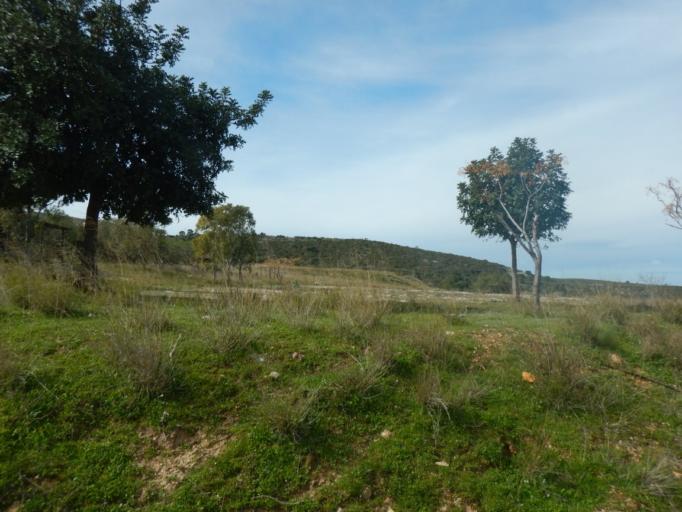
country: GR
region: Attica
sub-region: Nomos Piraios
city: Perama
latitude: 37.9748
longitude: 23.5924
